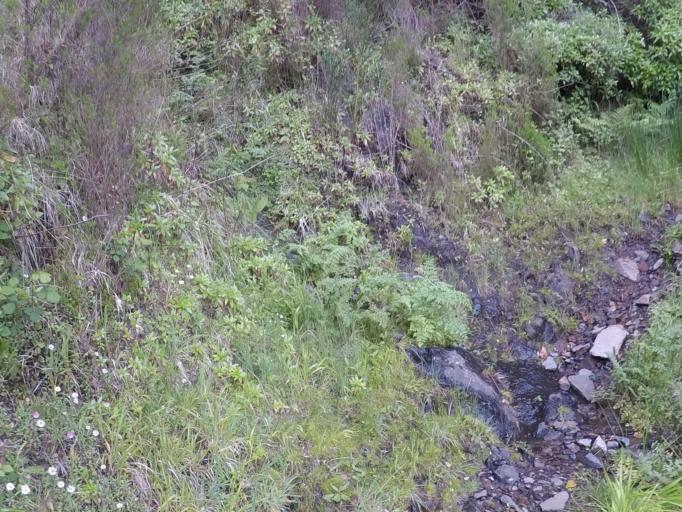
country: PT
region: Madeira
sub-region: Camara de Lobos
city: Curral das Freiras
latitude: 32.7353
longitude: -16.9923
